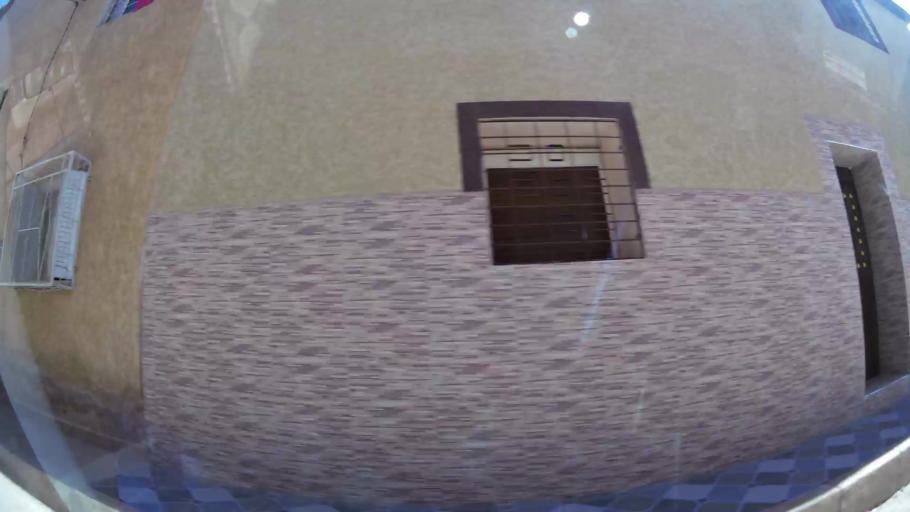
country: MA
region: Oriental
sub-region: Oujda-Angad
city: Oujda
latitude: 34.6560
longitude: -1.9040
